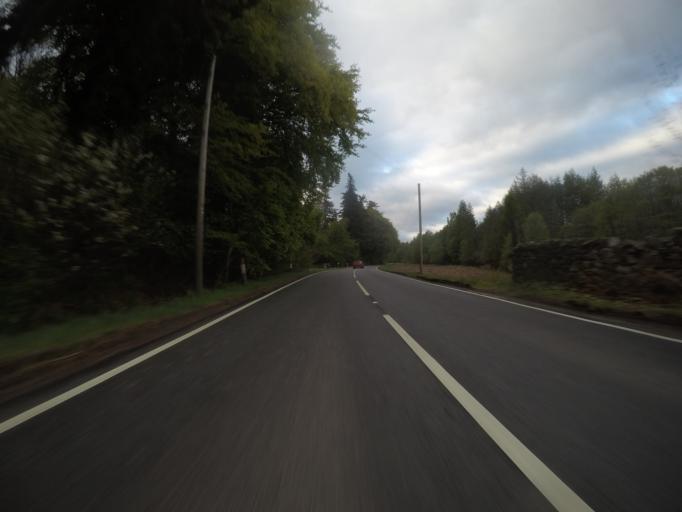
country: GB
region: Scotland
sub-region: Highland
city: Spean Bridge
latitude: 57.1059
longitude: -4.7198
